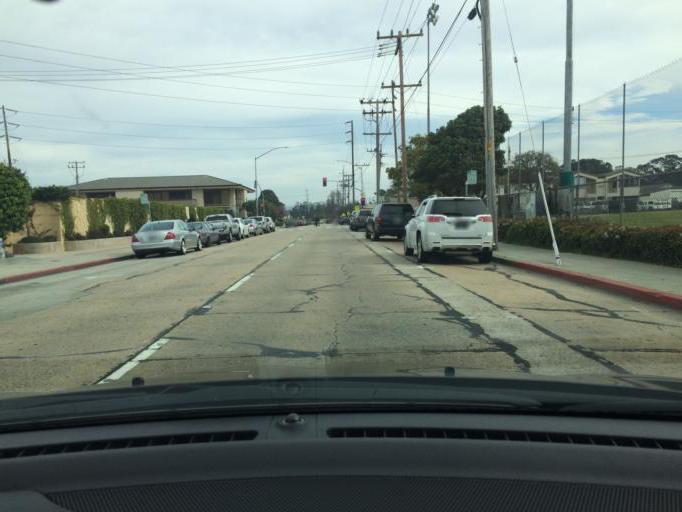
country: US
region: California
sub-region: Monterey County
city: Monterey
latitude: 36.5994
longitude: -121.8915
